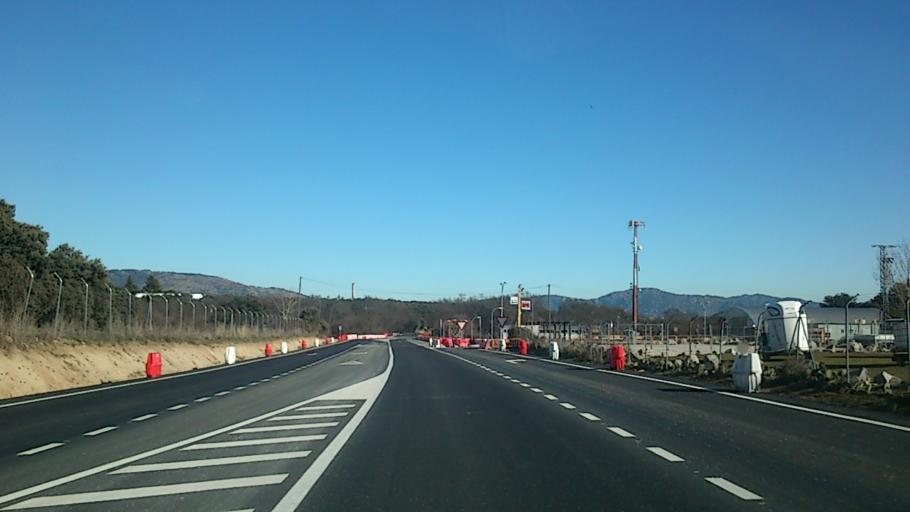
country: ES
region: Madrid
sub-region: Provincia de Madrid
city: Guadarrama
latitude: 40.6519
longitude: -4.0685
